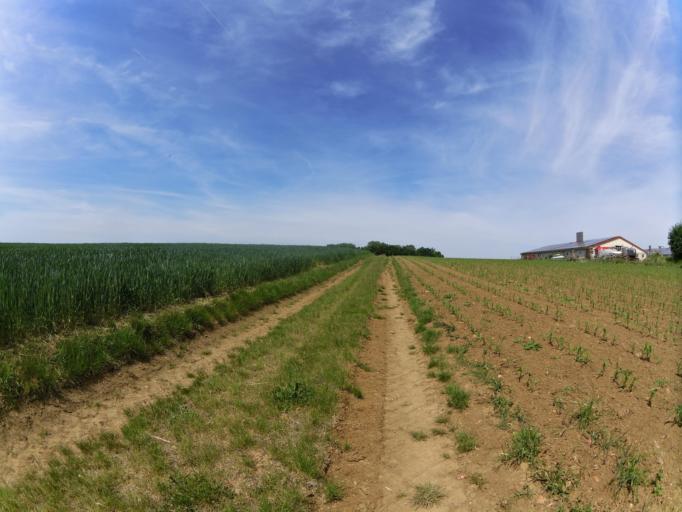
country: DE
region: Bavaria
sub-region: Regierungsbezirk Unterfranken
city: Sommerhausen
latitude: 49.6683
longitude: 10.0201
